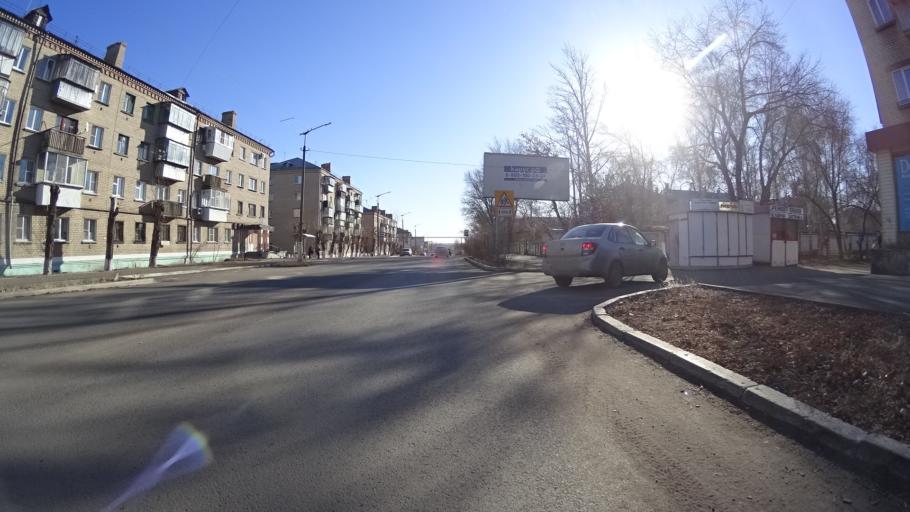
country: RU
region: Chelyabinsk
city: Troitsk
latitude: 54.0811
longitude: 61.5354
